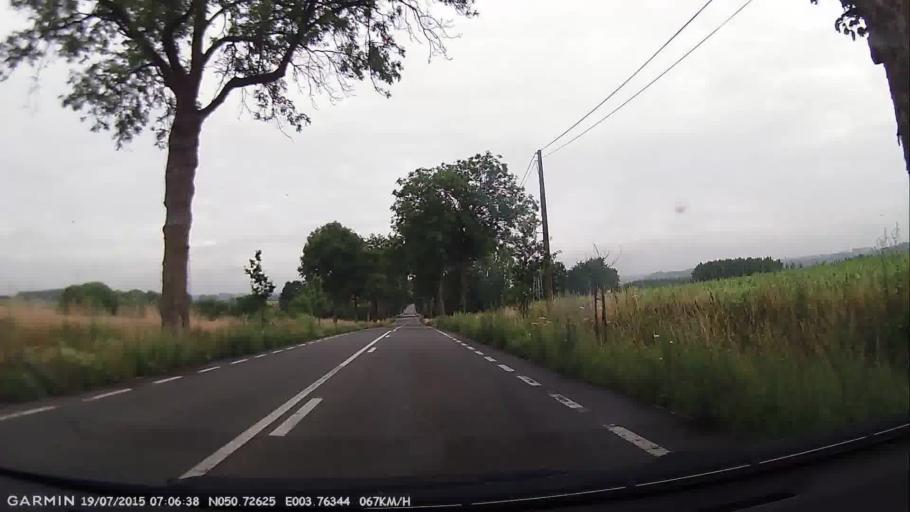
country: BE
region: Wallonia
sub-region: Province du Hainaut
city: Flobecq
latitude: 50.7263
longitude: 3.7632
